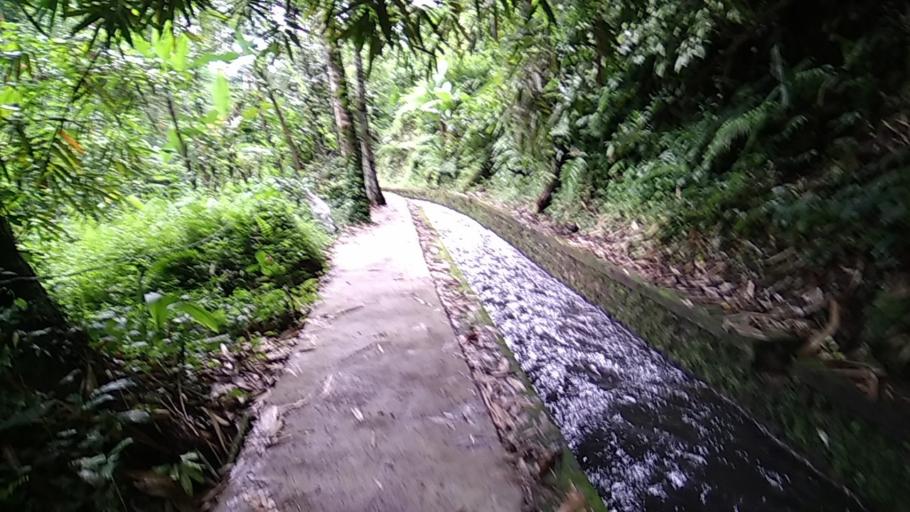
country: ID
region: Bali
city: Banjar Kubu
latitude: -8.4424
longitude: 115.3875
